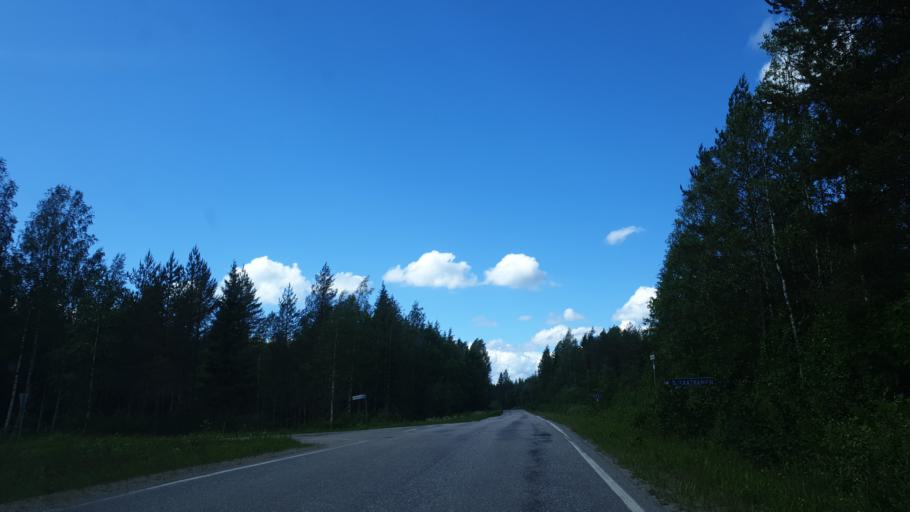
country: FI
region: Northern Savo
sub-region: Koillis-Savo
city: Kaavi
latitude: 63.0260
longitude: 28.6217
